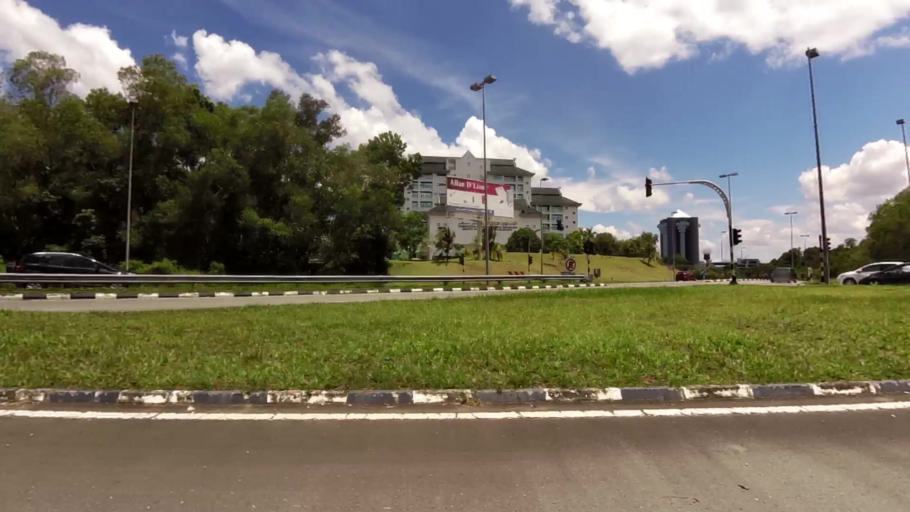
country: BN
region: Brunei and Muara
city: Bandar Seri Begawan
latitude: 4.9265
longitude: 114.9582
